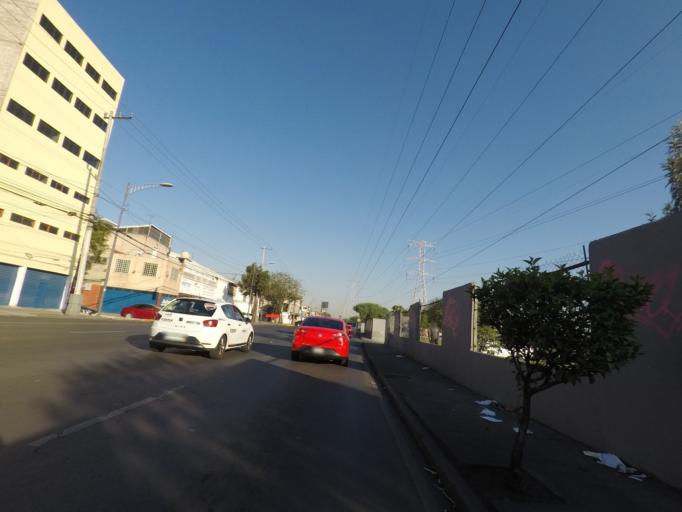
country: MX
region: Mexico City
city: Iztapalapa
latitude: 19.3674
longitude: -99.0731
